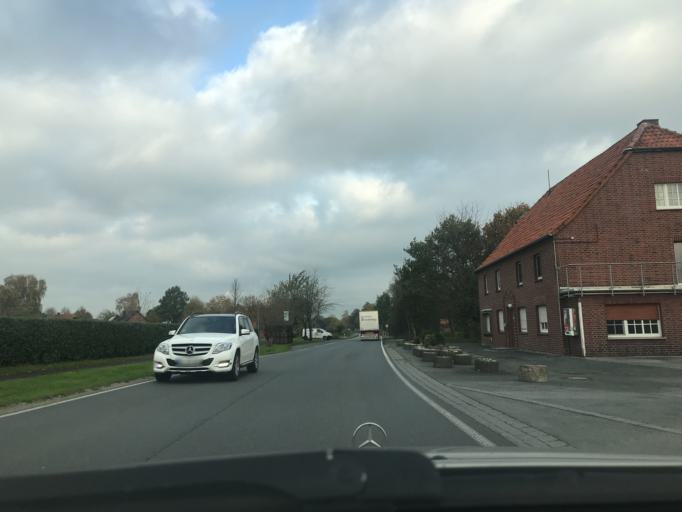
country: DE
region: North Rhine-Westphalia
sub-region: Regierungsbezirk Arnsberg
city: Welver
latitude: 51.6525
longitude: 8.0418
